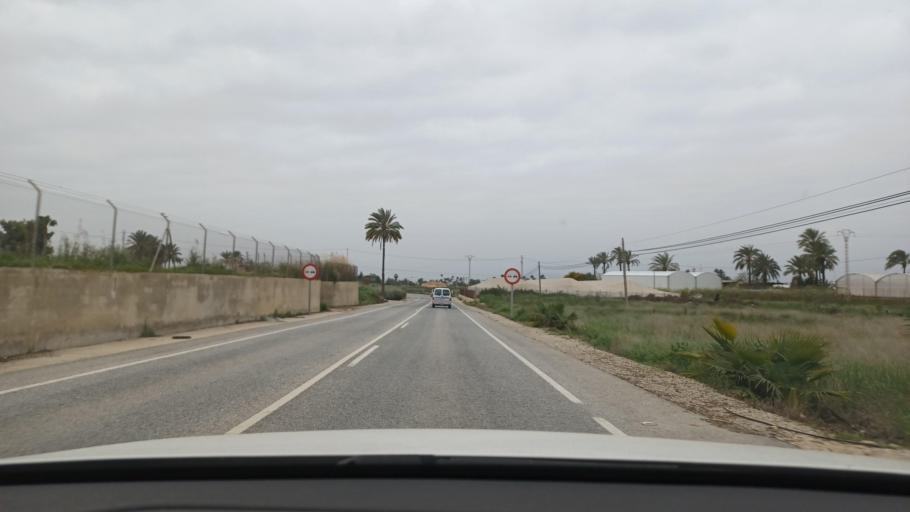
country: ES
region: Valencia
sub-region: Provincia de Alicante
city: Elche
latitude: 38.2379
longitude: -0.7126
